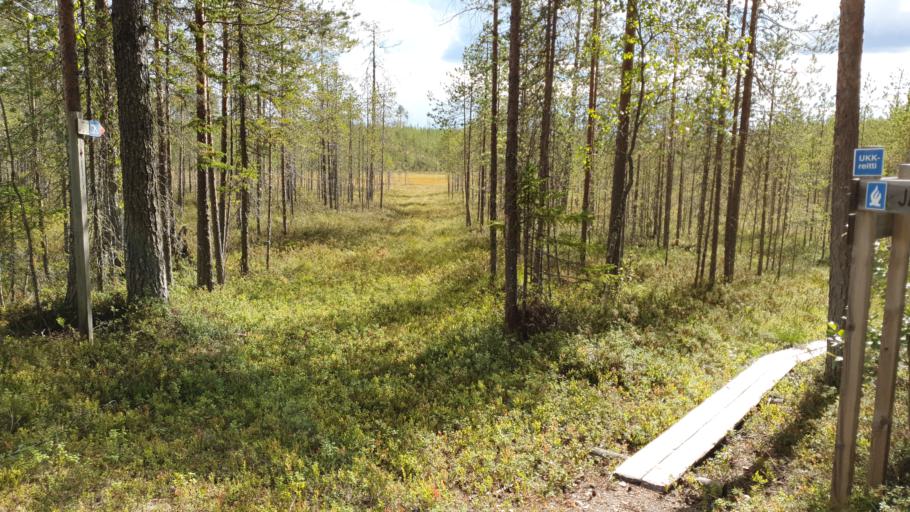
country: FI
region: Kainuu
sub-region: Kehys-Kainuu
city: Kuhmo
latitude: 64.0836
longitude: 29.5247
